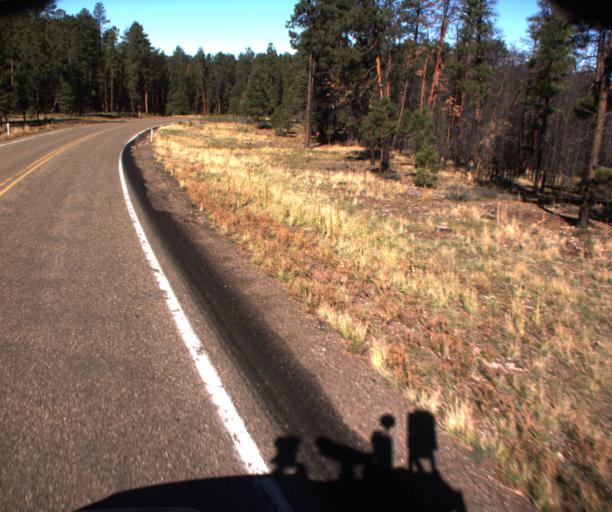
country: US
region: Arizona
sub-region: Coconino County
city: Fredonia
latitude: 36.7351
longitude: -112.2252
